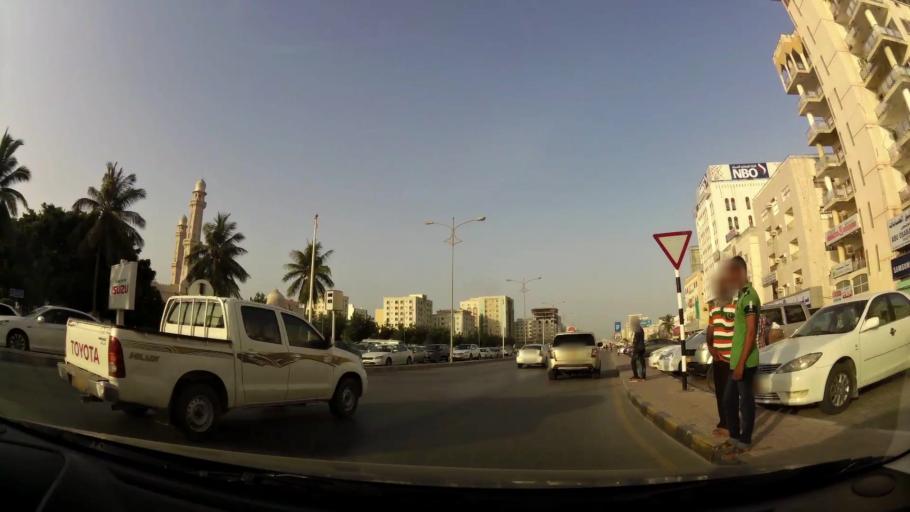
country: OM
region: Zufar
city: Salalah
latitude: 17.0157
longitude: 54.0933
